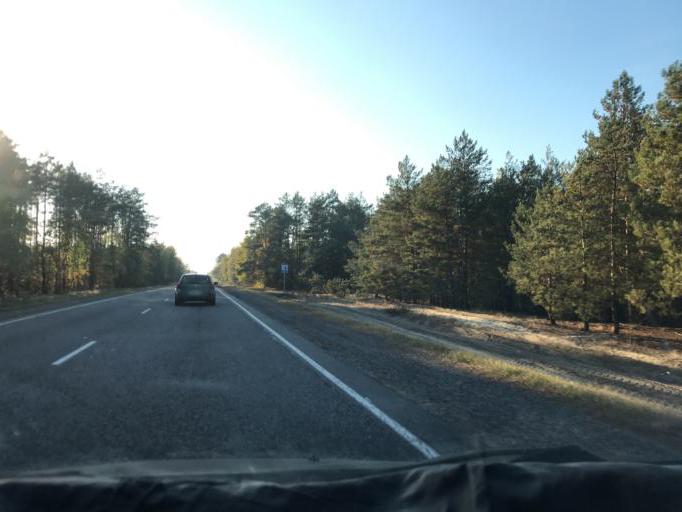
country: BY
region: Gomel
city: Zhytkavichy
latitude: 52.2708
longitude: 27.9876
